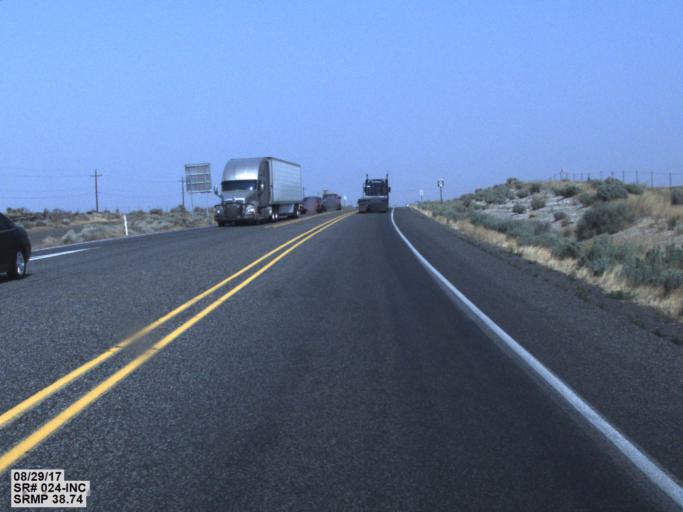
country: US
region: Washington
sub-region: Grant County
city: Desert Aire
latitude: 46.5778
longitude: -119.7283
